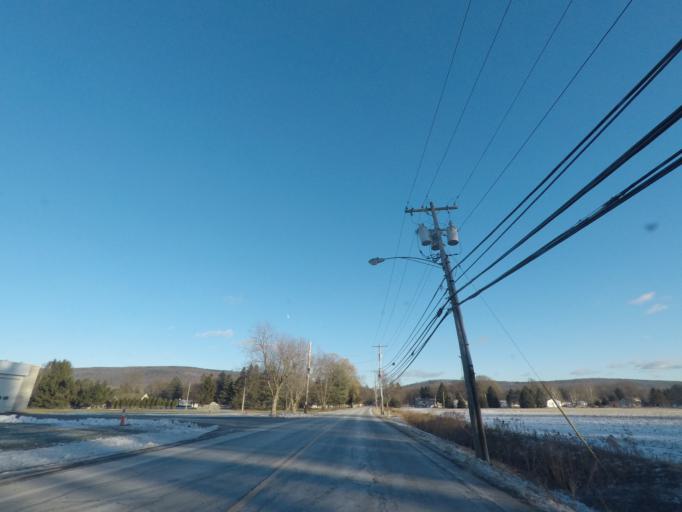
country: US
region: New York
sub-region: Rensselaer County
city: Poestenkill
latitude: 42.6958
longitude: -73.5786
